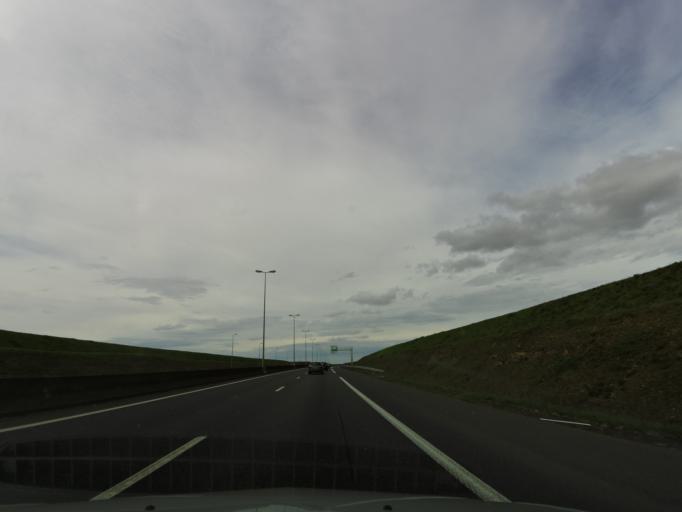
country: FR
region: Lower Normandy
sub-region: Departement du Calvados
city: Eterville
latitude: 49.1478
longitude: -0.4115
